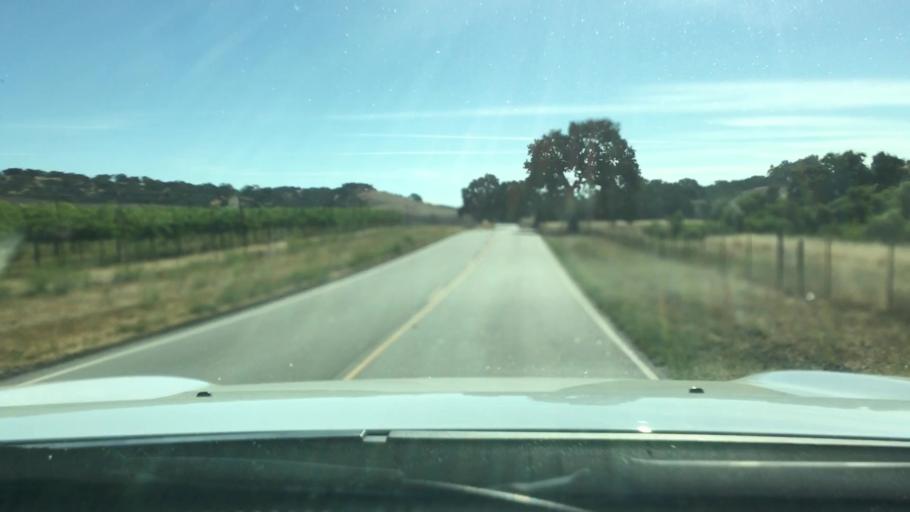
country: US
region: California
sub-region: San Luis Obispo County
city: Templeton
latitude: 35.5631
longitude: -120.6627
